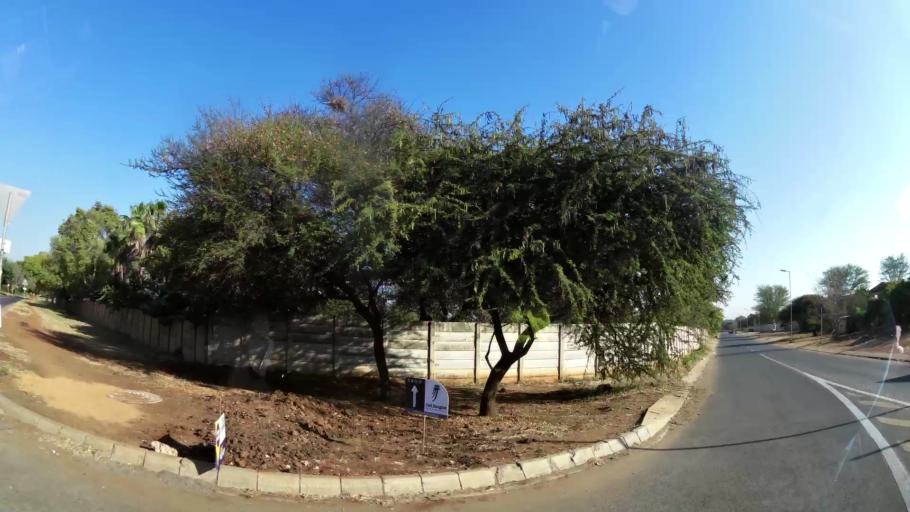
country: ZA
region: Gauteng
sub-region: City of Tshwane Metropolitan Municipality
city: Pretoria
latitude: -25.6727
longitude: 28.2133
